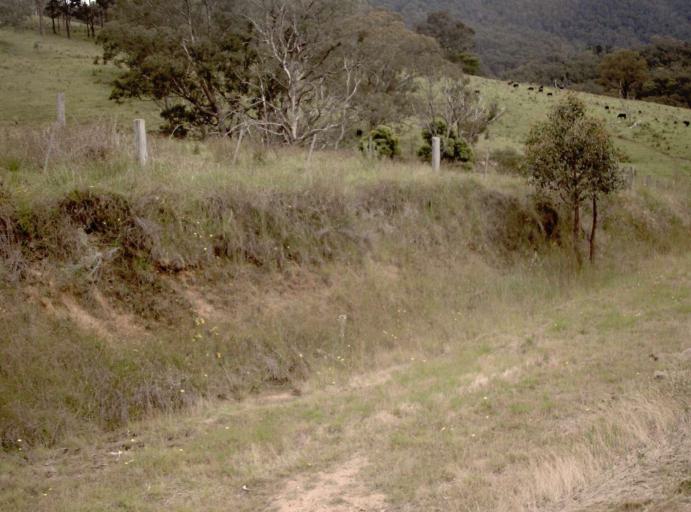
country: AU
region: Victoria
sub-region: East Gippsland
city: Bairnsdale
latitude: -37.5868
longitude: 147.1839
